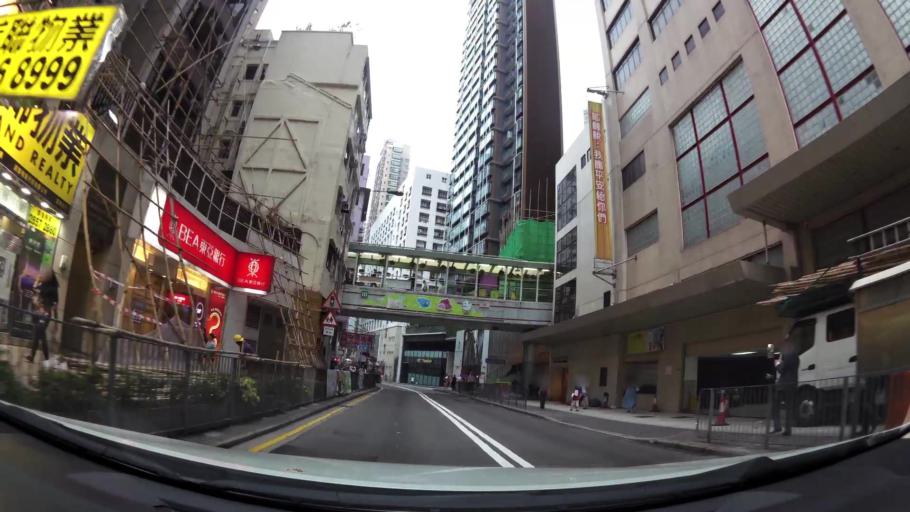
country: HK
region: Central and Western
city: Central
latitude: 22.2813
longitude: 114.1520
